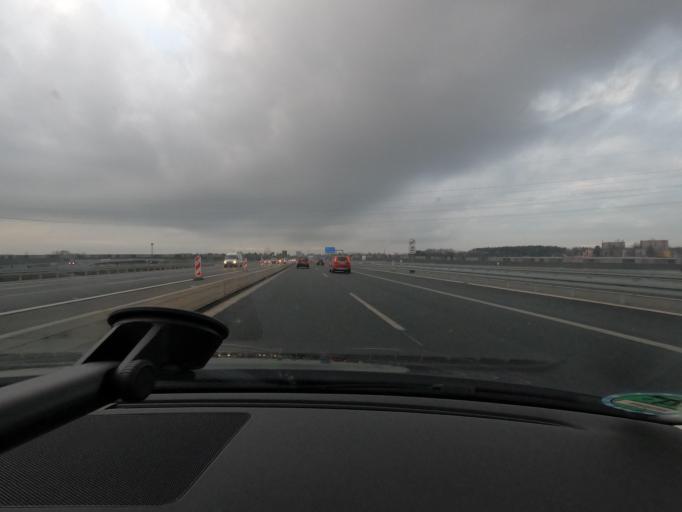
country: DE
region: Bavaria
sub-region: Regierungsbezirk Mittelfranken
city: Erlangen
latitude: 49.5572
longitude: 10.9924
